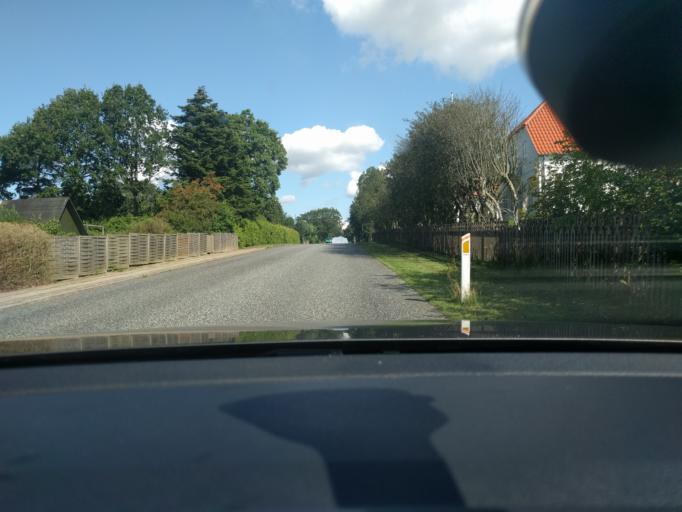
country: DK
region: Central Jutland
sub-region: Viborg Kommune
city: Viborg
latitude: 56.5502
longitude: 9.4011
